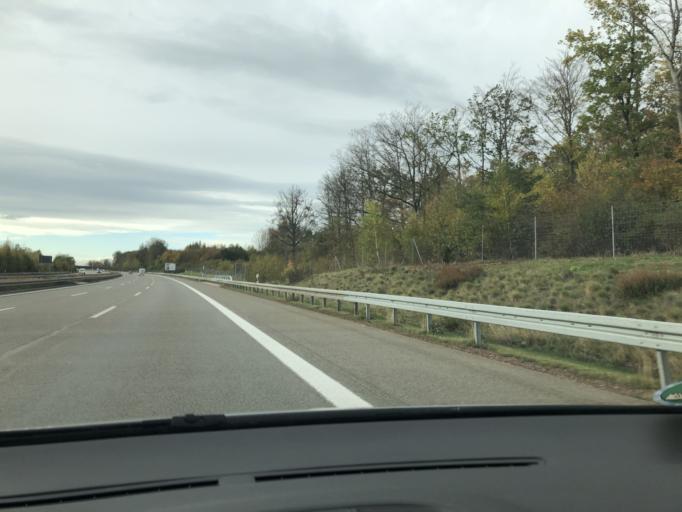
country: DE
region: Saxony
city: Hohenstein-Ernstthal
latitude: 50.8131
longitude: 12.6870
